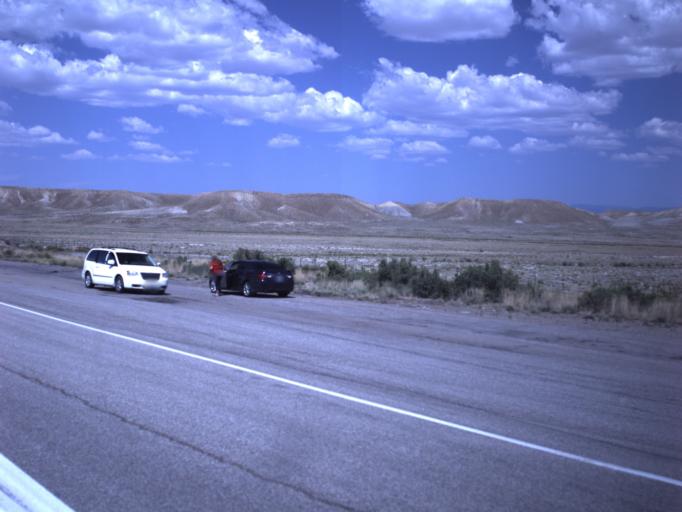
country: US
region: Utah
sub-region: Carbon County
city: Price
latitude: 39.4558
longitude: -110.8611
